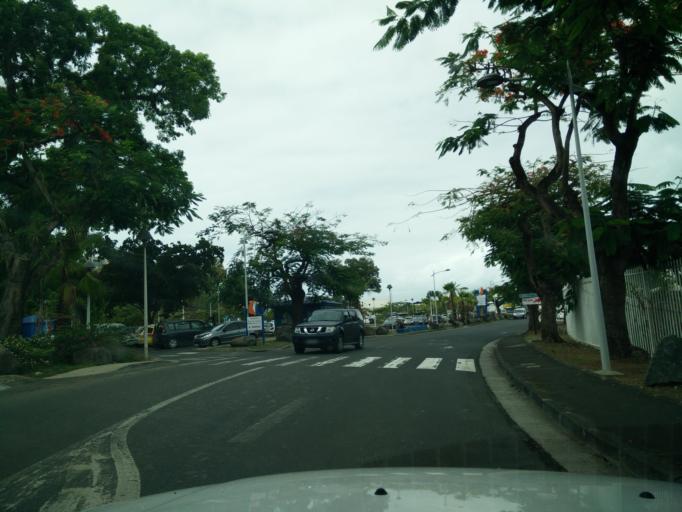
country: GP
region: Guadeloupe
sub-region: Guadeloupe
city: Pointe-a-Pitre
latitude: 16.2213
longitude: -61.5268
